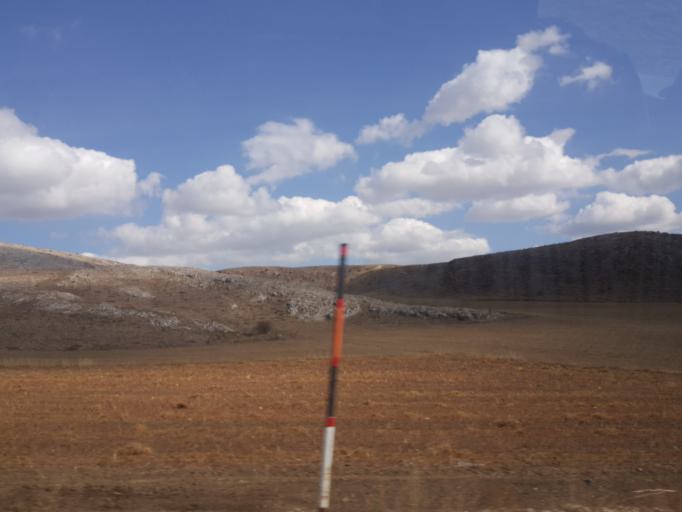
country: TR
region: Tokat
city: Artova
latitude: 40.1336
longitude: 36.3502
